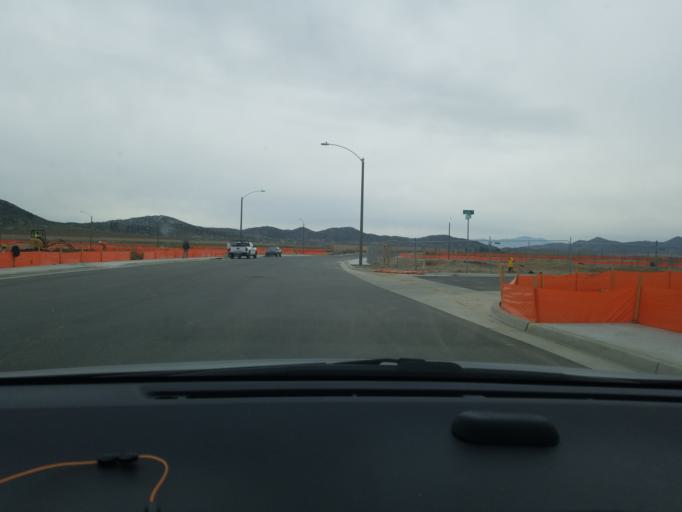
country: US
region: California
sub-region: Riverside County
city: Winchester
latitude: 33.6946
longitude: -117.1012
